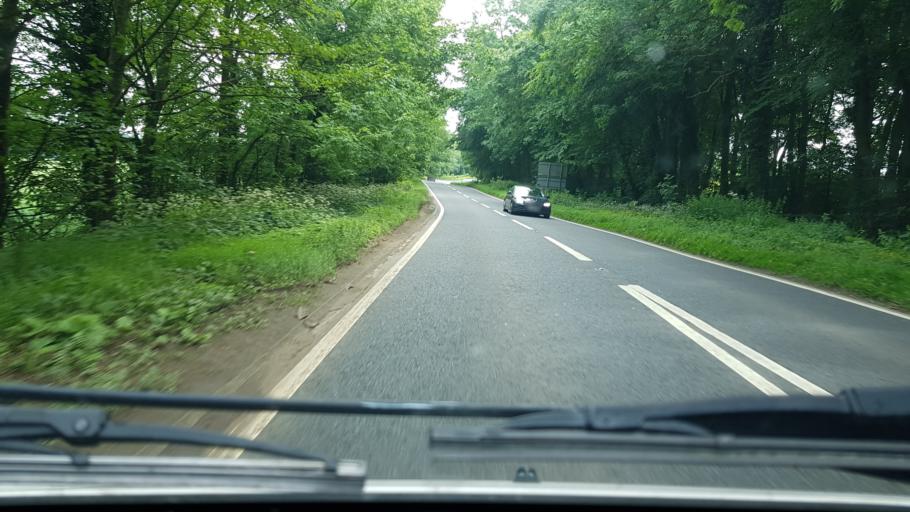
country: GB
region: England
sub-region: Worcestershire
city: Broadway
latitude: 52.0289
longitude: -1.8250
